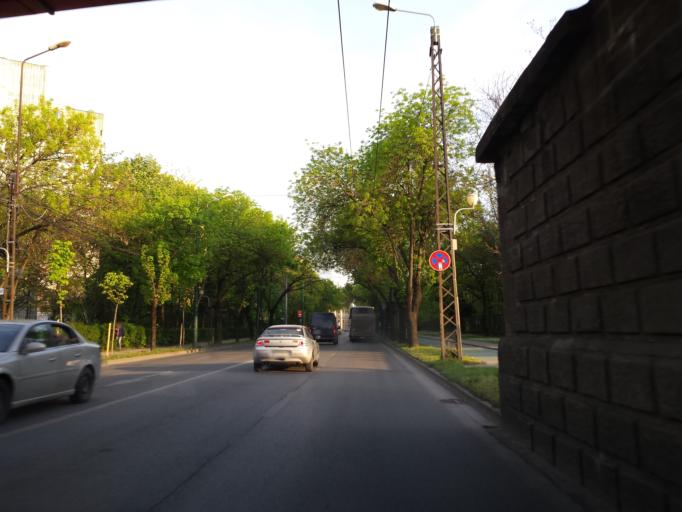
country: RO
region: Timis
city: Timisoara
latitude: 45.7622
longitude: 21.2264
